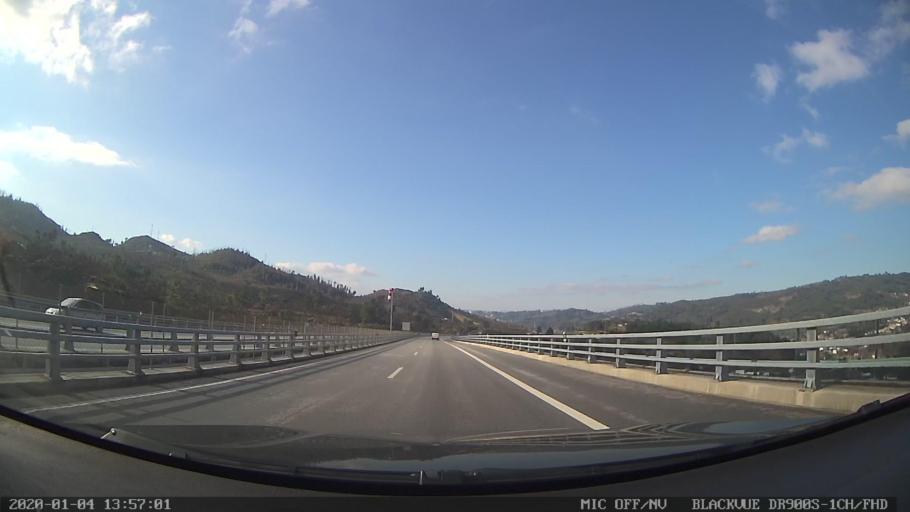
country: PT
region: Porto
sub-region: Amarante
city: Amarante
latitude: 41.2587
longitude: -8.0008
